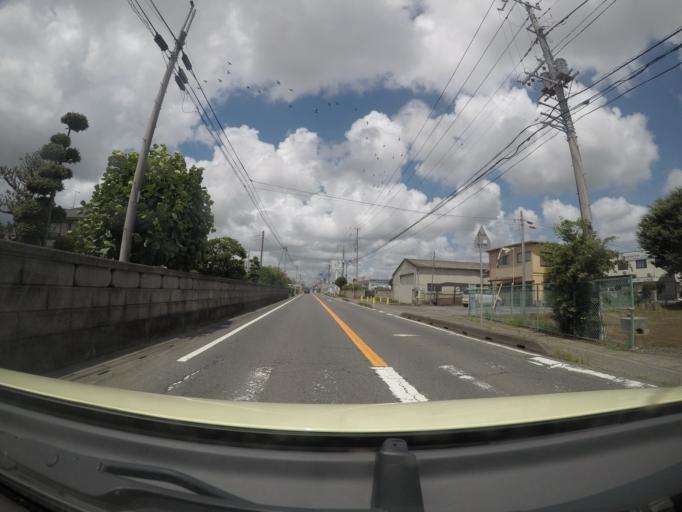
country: JP
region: Ibaraki
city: Mitsukaido
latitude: 36.0398
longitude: 139.9881
